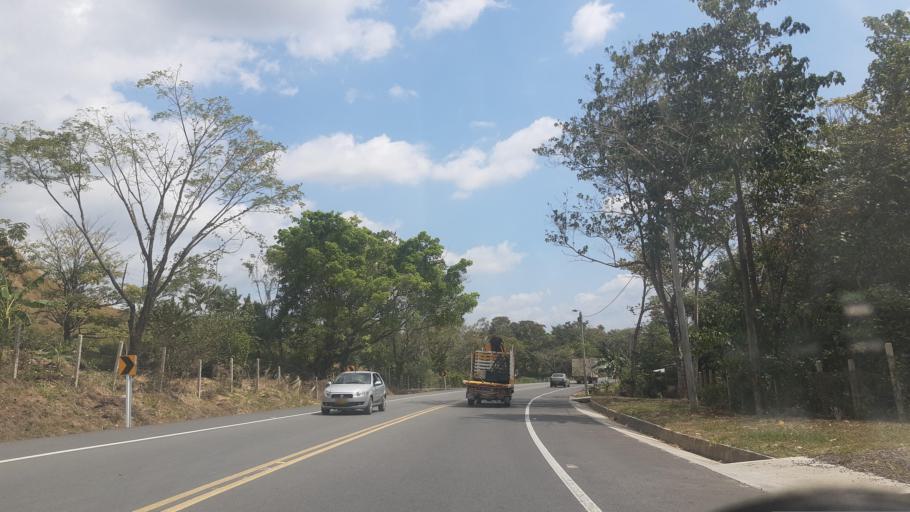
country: CO
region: Casanare
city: Tauramena
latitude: 5.0207
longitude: -72.6650
